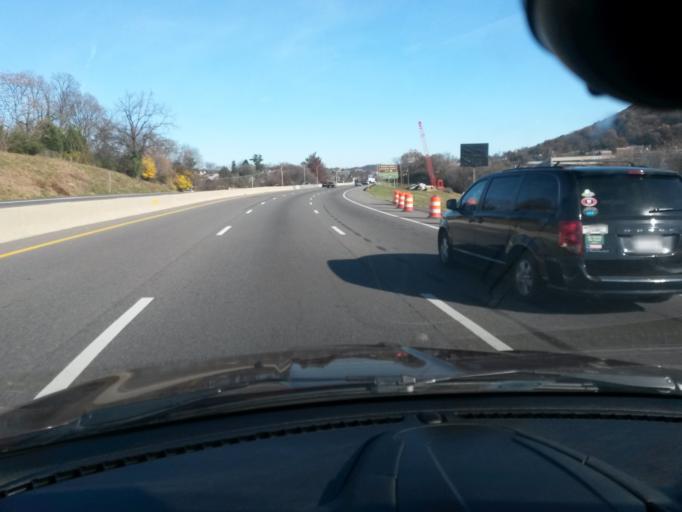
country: US
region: Virginia
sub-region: City of Roanoke
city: Roanoke
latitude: 37.2581
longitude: -79.9496
